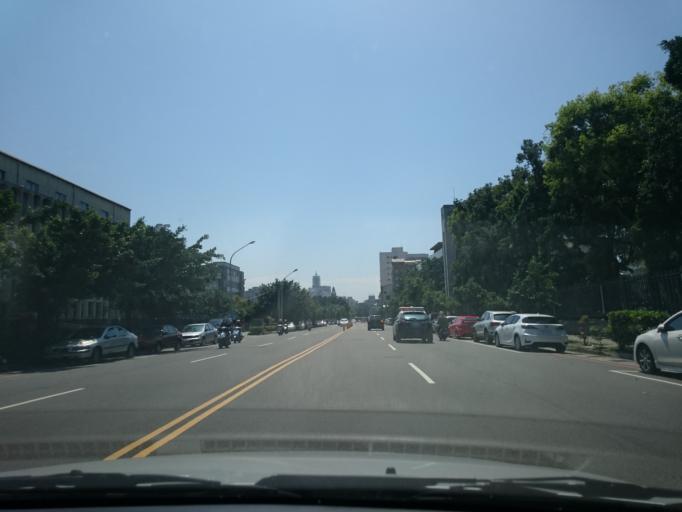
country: TW
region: Taiwan
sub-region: Taichung City
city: Taichung
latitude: 24.1504
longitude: 120.6878
